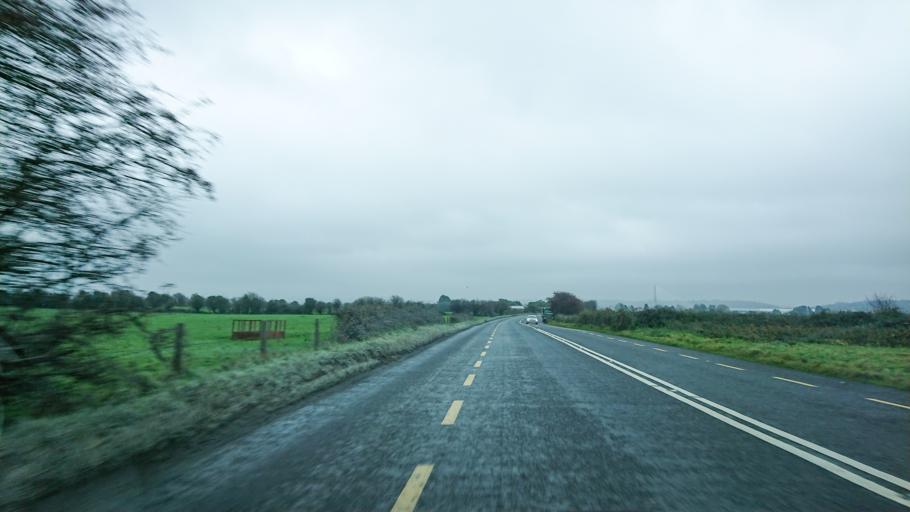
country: IE
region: Leinster
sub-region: Kilkenny
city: Mooncoin
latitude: 52.2825
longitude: -7.1861
